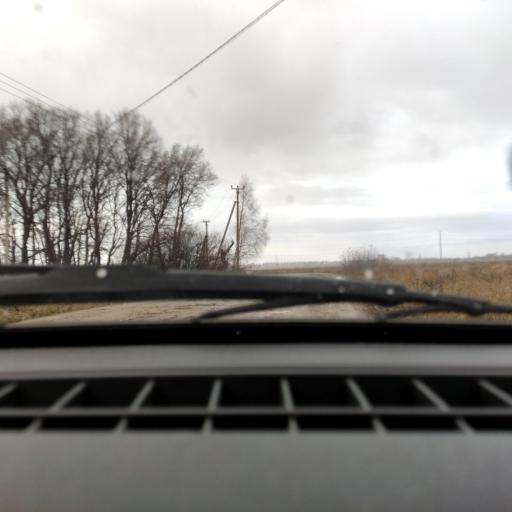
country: RU
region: Bashkortostan
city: Iglino
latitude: 54.7390
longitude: 56.3247
